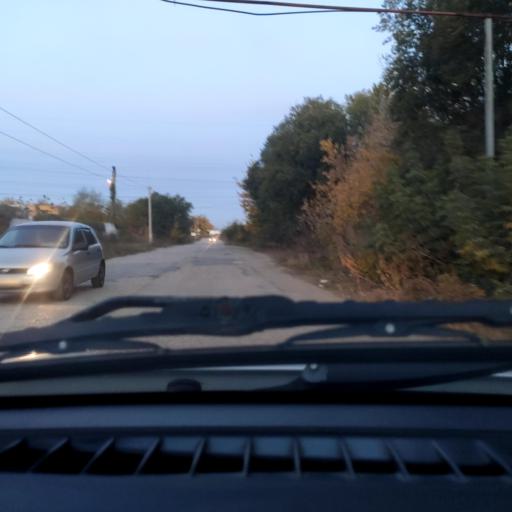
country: RU
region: Samara
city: Tol'yatti
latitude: 53.5473
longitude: 49.4460
